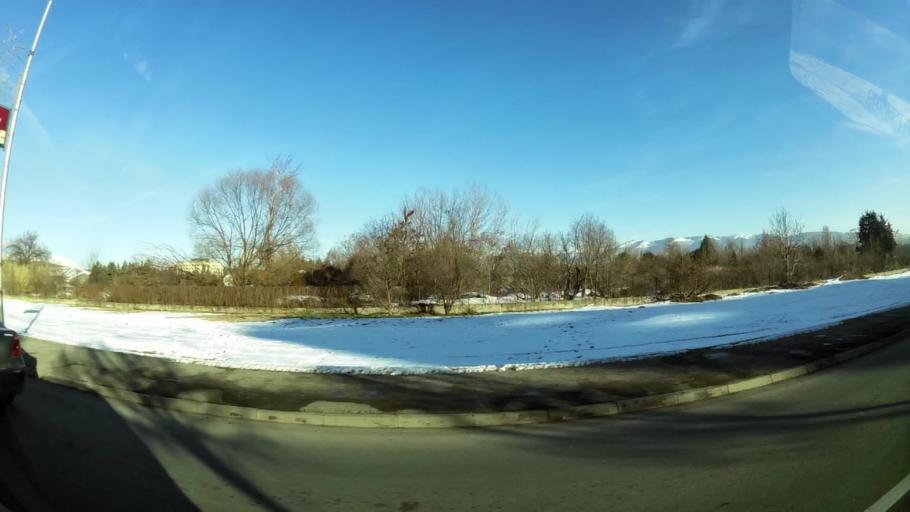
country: MK
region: Karpos
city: Skopje
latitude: 42.0070
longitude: 21.4081
